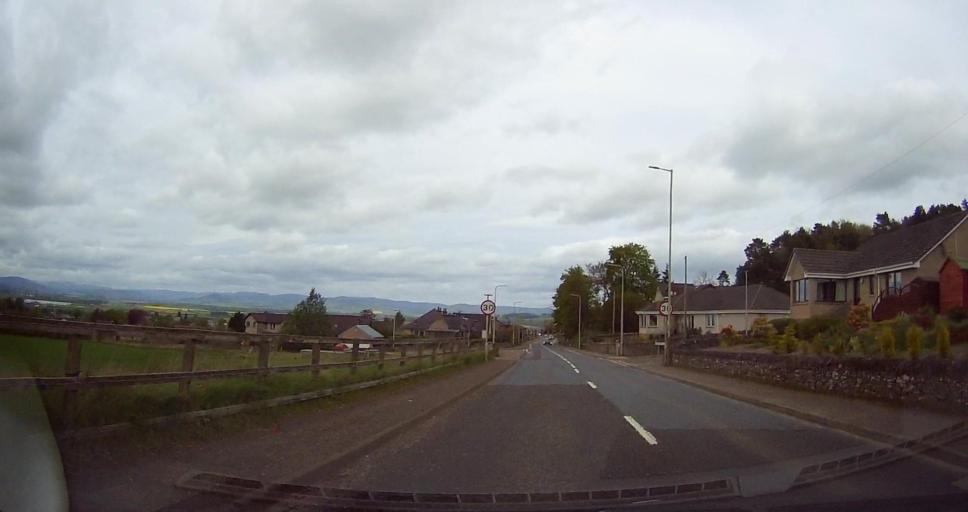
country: GB
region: Scotland
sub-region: Angus
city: Forfar
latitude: 56.6302
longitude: -2.8966
